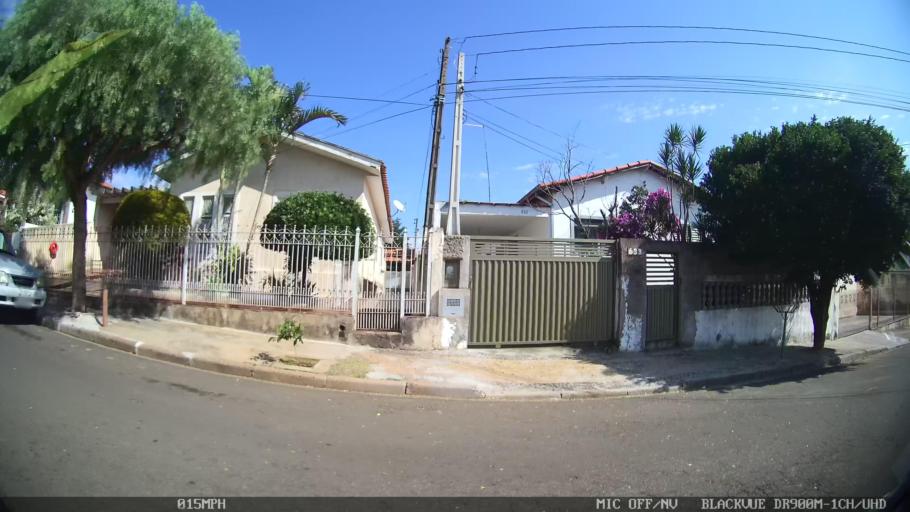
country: BR
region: Sao Paulo
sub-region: Americana
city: Americana
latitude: -22.7221
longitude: -47.3029
